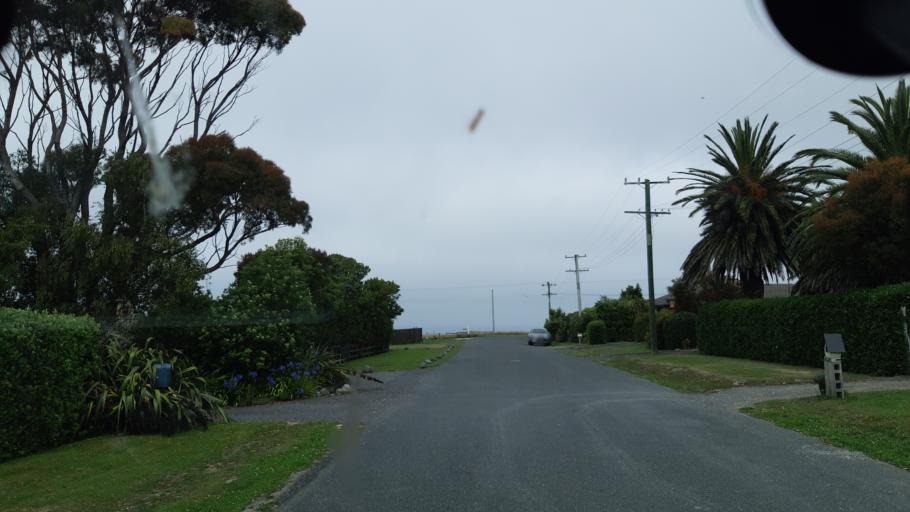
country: NZ
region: Canterbury
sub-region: Kaikoura District
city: Kaikoura
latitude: -42.4181
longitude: 173.6992
